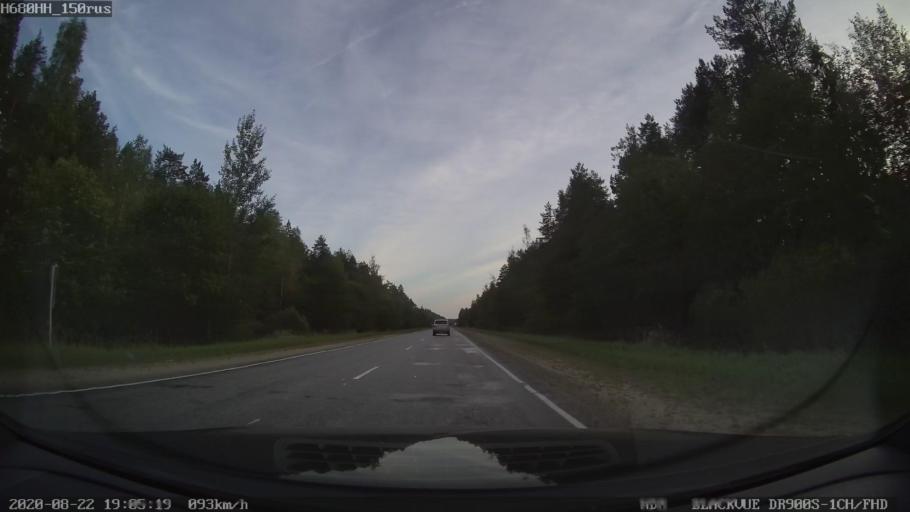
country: RU
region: Tverskaya
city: Sakharovo
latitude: 57.0782
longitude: 36.1124
